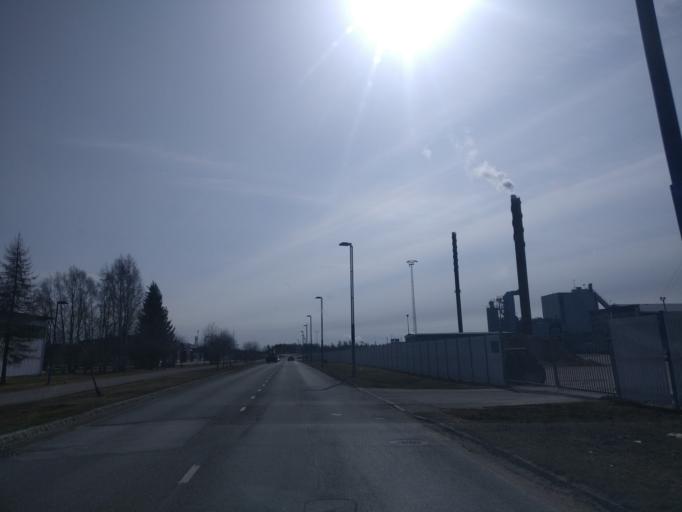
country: FI
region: Lapland
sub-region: Kemi-Tornio
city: Kemi
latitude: 65.7356
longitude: 24.5824
